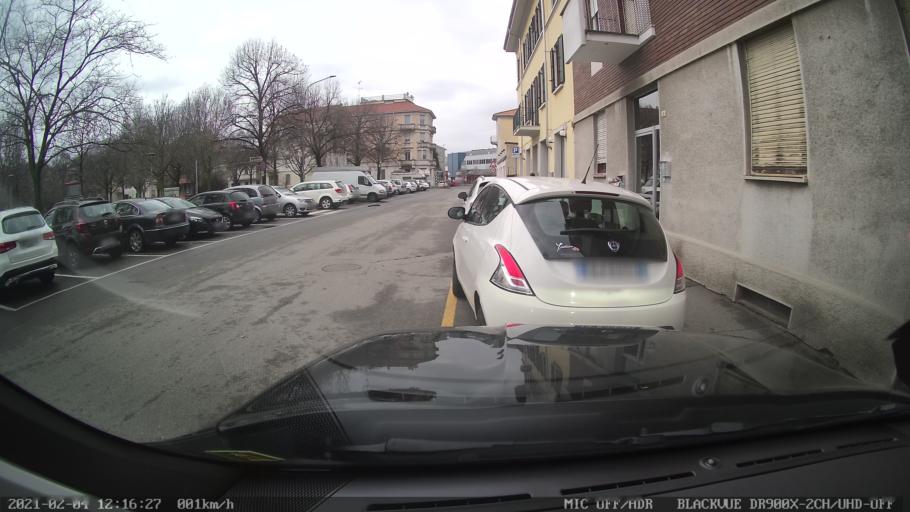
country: IT
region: Piedmont
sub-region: Provincia di Novara
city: Novara
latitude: 45.4491
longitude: 8.6112
